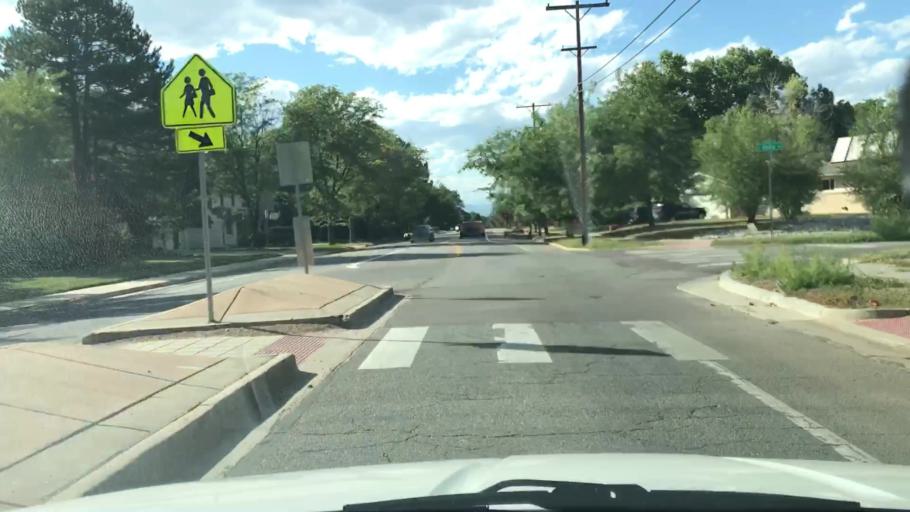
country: US
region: Colorado
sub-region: Arapahoe County
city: Cherry Hills Village
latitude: 39.6460
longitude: -104.9225
